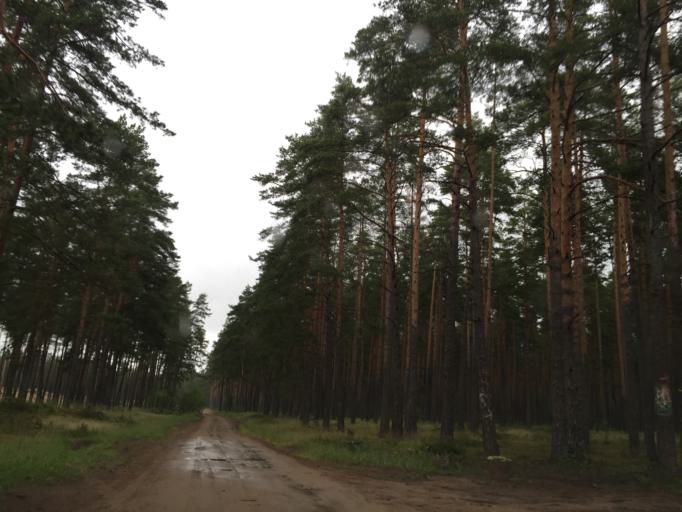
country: LV
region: Riga
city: Jaunciems
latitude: 57.0569
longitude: 24.2021
